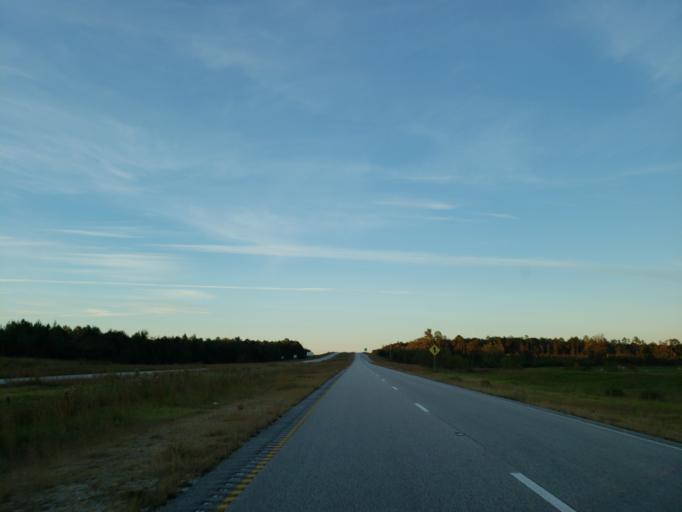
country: US
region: Mississippi
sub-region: Wayne County
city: Belmont
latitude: 31.4372
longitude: -88.4654
